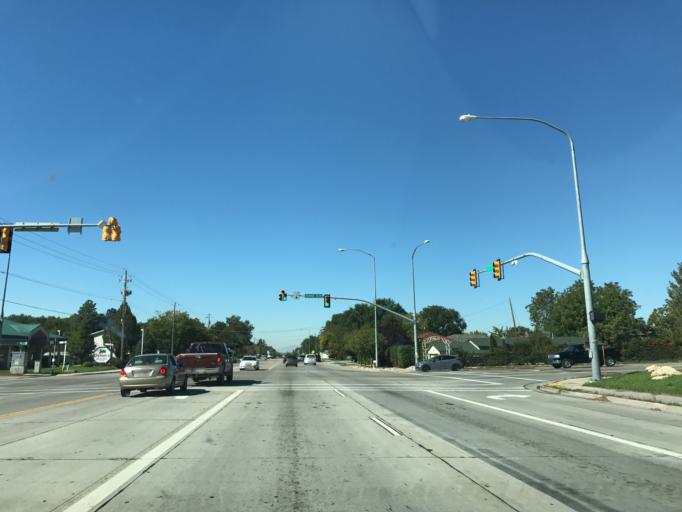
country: US
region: Utah
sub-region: Weber County
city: Ogden
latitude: 41.2441
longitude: -111.9528
